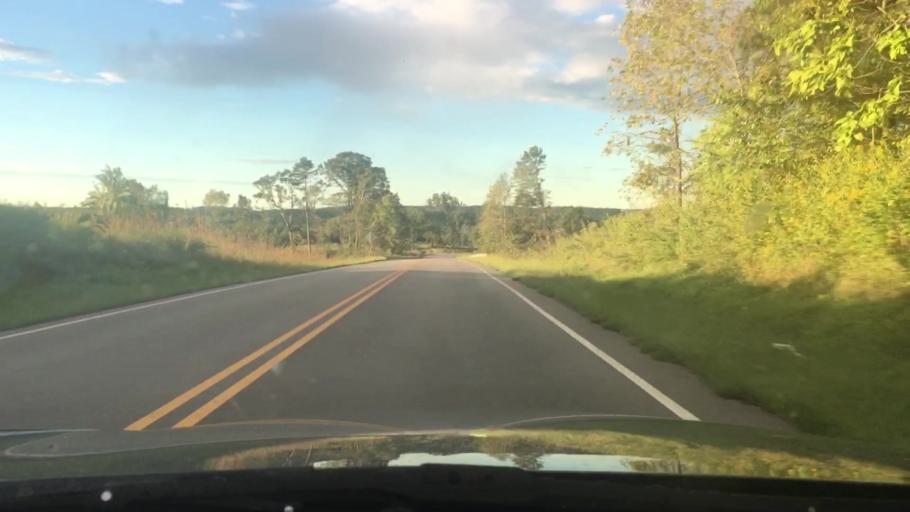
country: US
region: North Carolina
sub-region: Caswell County
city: Yanceyville
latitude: 36.3978
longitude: -79.3296
